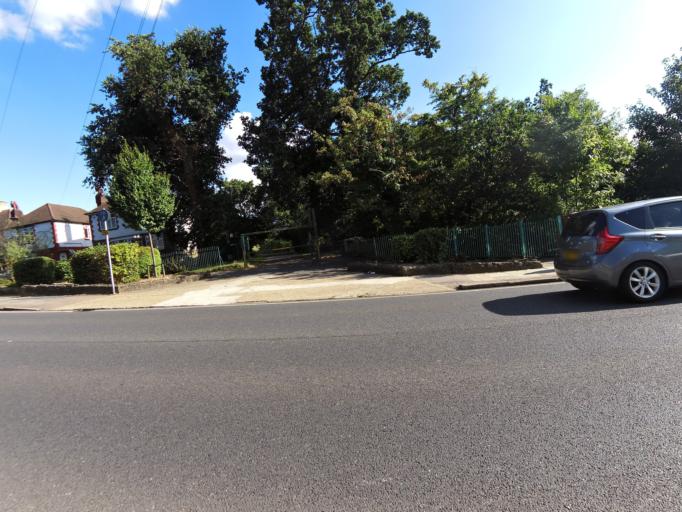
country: GB
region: England
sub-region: Greater London
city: Wood Green
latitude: 51.6317
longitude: -0.1452
